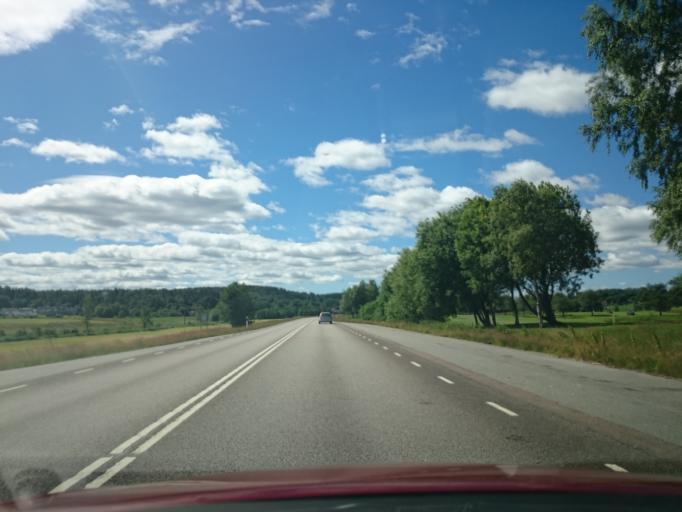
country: SE
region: Vaestra Goetaland
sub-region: Lerums Kommun
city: Olstorp
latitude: 57.8315
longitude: 12.2549
